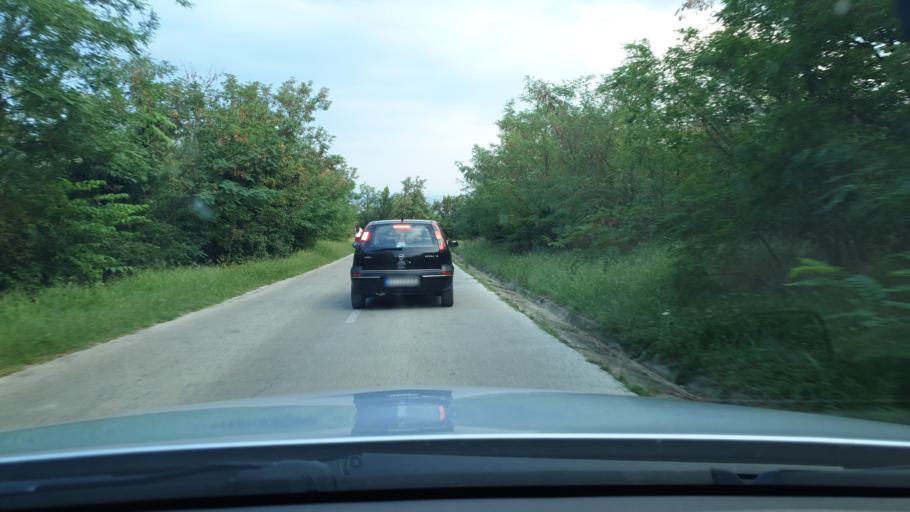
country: RS
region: Autonomna Pokrajina Vojvodina
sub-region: Juznobanatski Okrug
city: Vrsac
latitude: 45.1192
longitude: 21.3250
